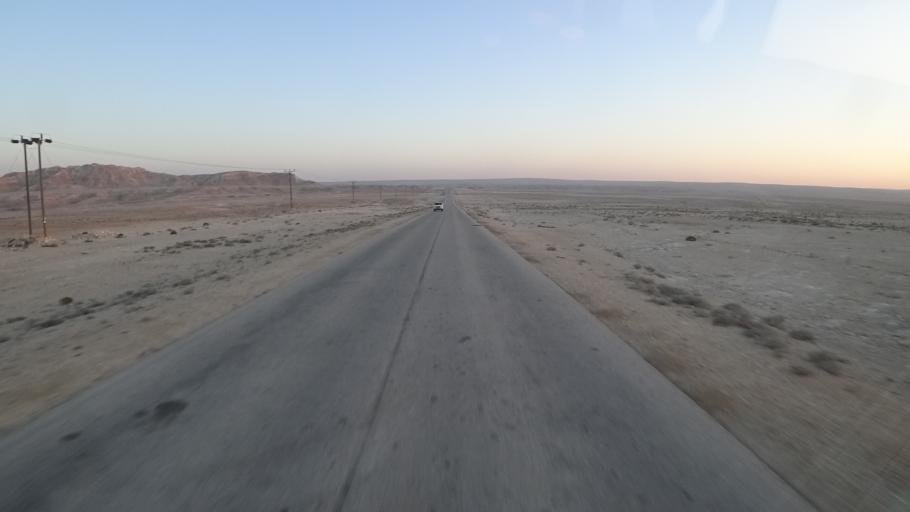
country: YE
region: Al Mahrah
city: Hawf
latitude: 16.9327
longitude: 53.3775
